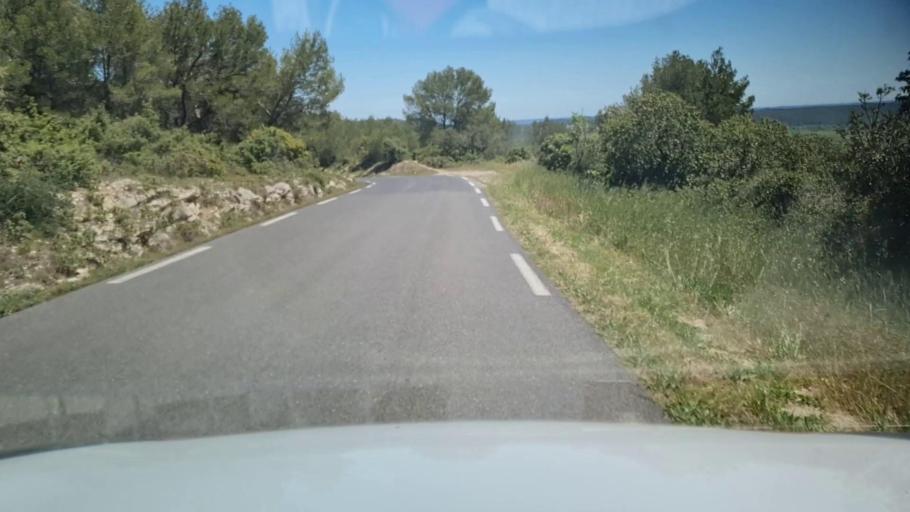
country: FR
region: Languedoc-Roussillon
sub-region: Departement du Gard
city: Clarensac
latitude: 43.8364
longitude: 4.2244
